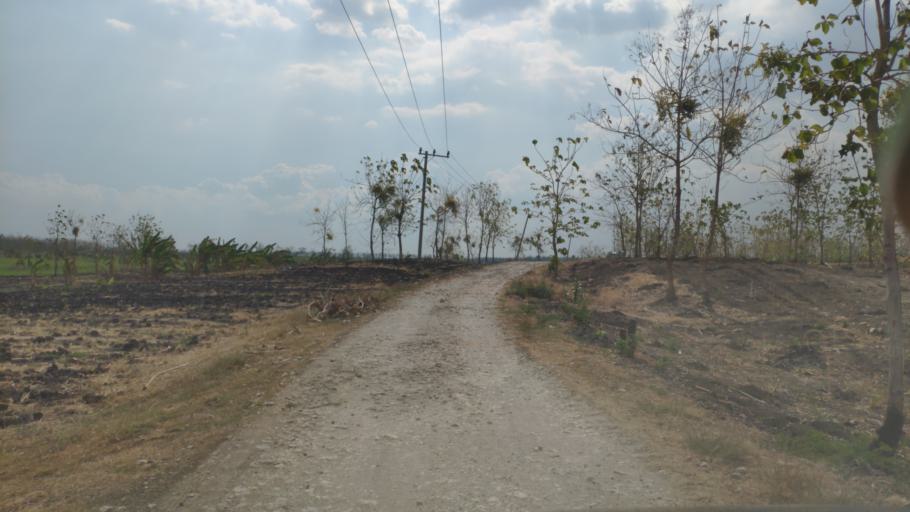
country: ID
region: Central Java
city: Mendenrejo
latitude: -7.3185
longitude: 111.3751
